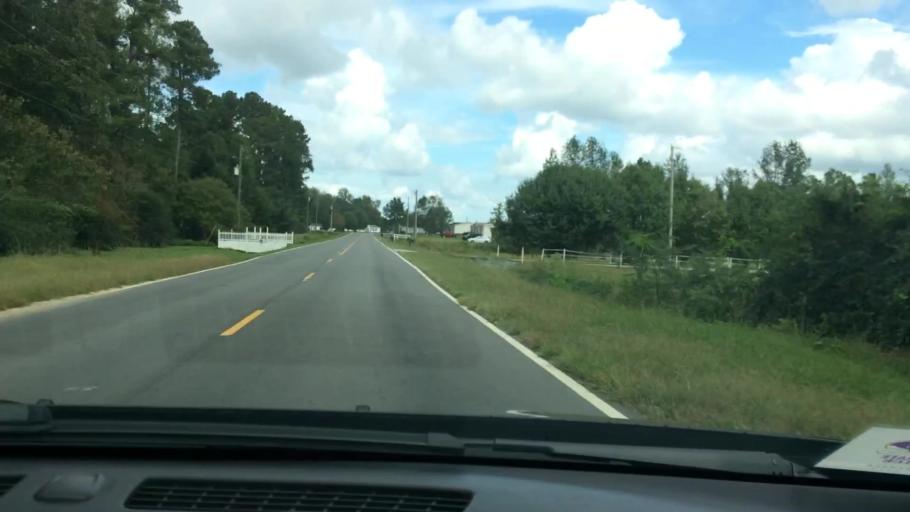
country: US
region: North Carolina
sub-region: Pitt County
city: Ayden
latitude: 35.4618
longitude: -77.4660
